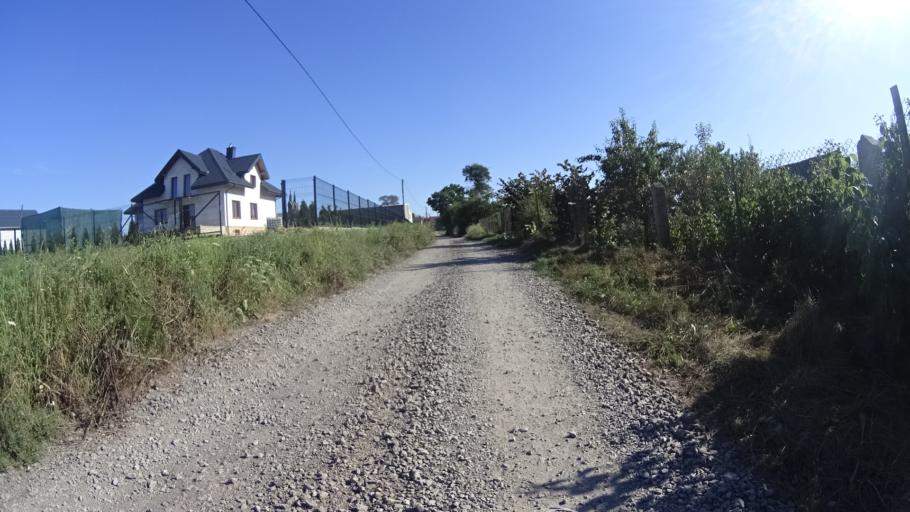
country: PL
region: Masovian Voivodeship
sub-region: Powiat bialobrzeski
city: Wysmierzyce
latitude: 51.6666
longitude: 20.8494
